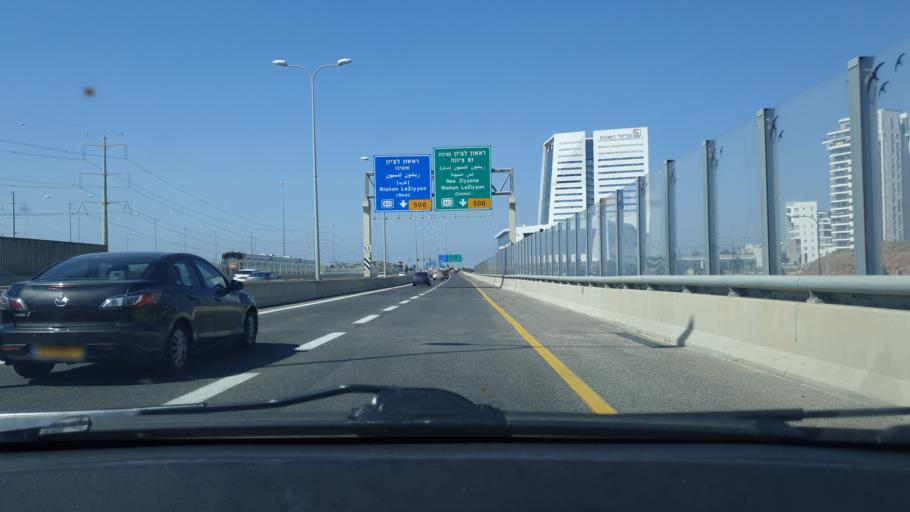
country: IL
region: Central District
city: Ness Ziona
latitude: 31.9480
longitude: 34.8069
